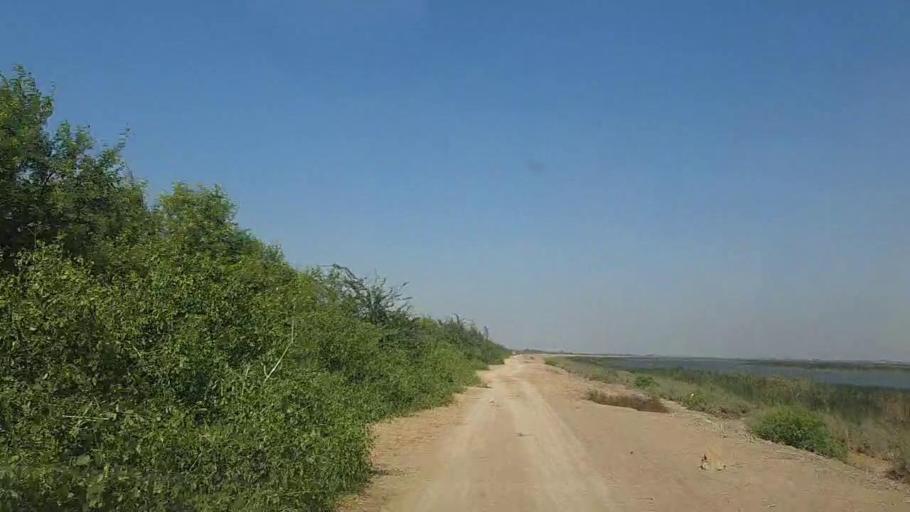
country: PK
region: Sindh
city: Daro Mehar
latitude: 24.9179
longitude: 68.0784
